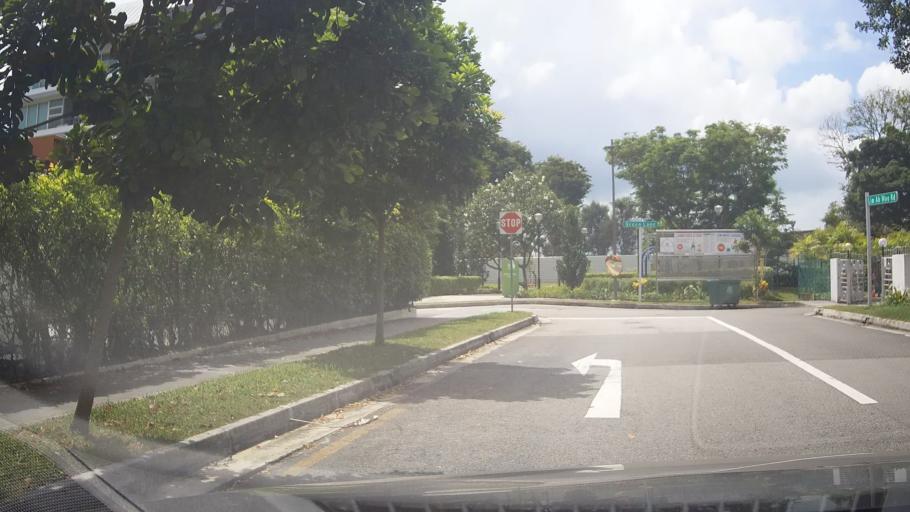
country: SG
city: Singapore
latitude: 1.3115
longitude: 103.8921
